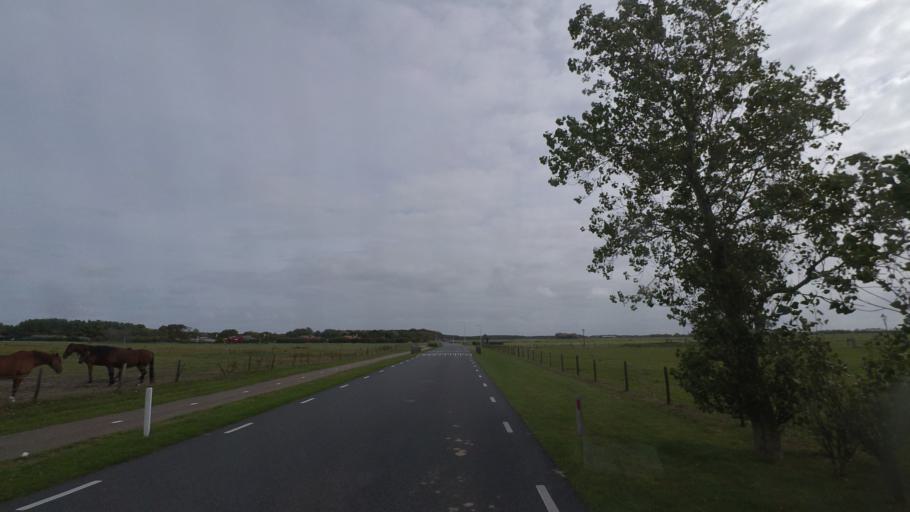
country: NL
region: Friesland
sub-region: Gemeente Ameland
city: Hollum
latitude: 53.4467
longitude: 5.6900
